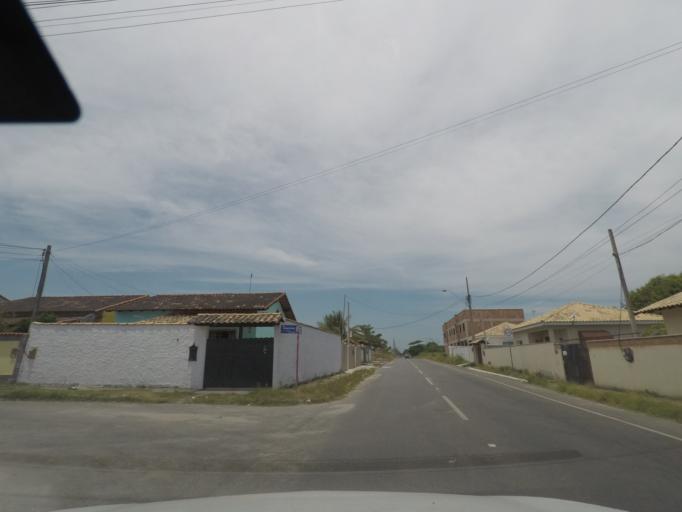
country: BR
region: Rio de Janeiro
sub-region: Marica
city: Marica
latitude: -22.9689
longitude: -42.9514
